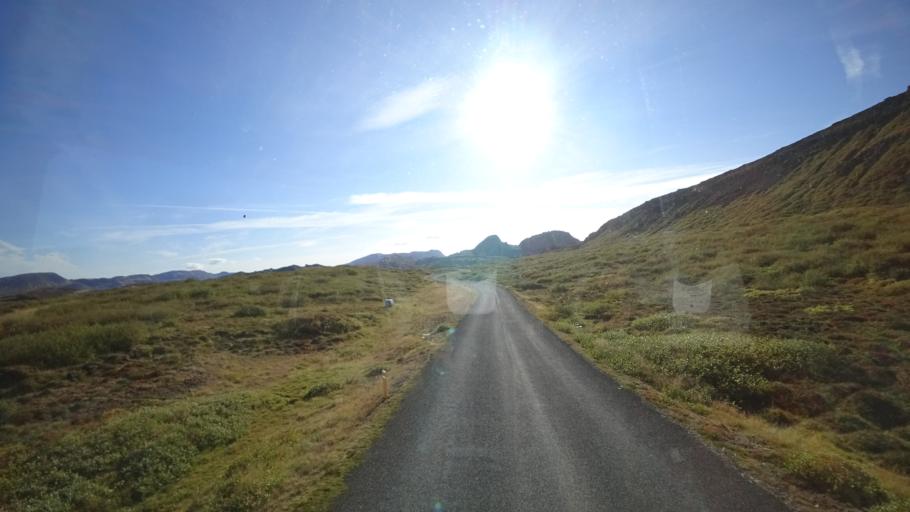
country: IS
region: South
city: Hveragerdi
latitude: 64.1620
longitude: -21.2456
